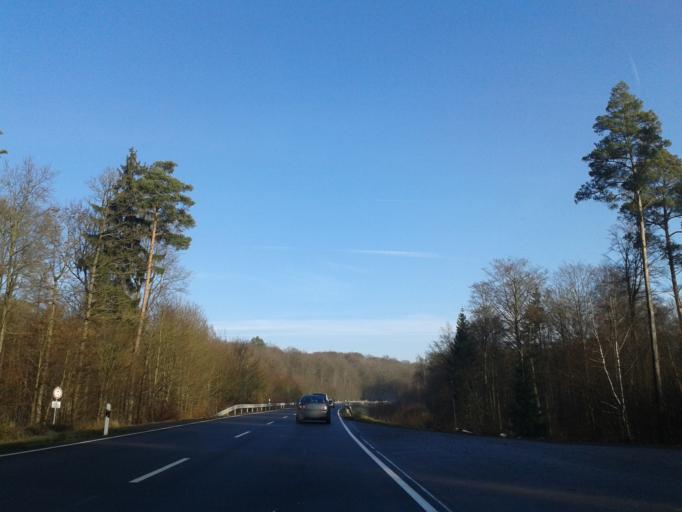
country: DE
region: Bavaria
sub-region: Regierungsbezirk Unterfranken
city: Aidhausen
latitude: 50.1064
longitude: 10.4155
